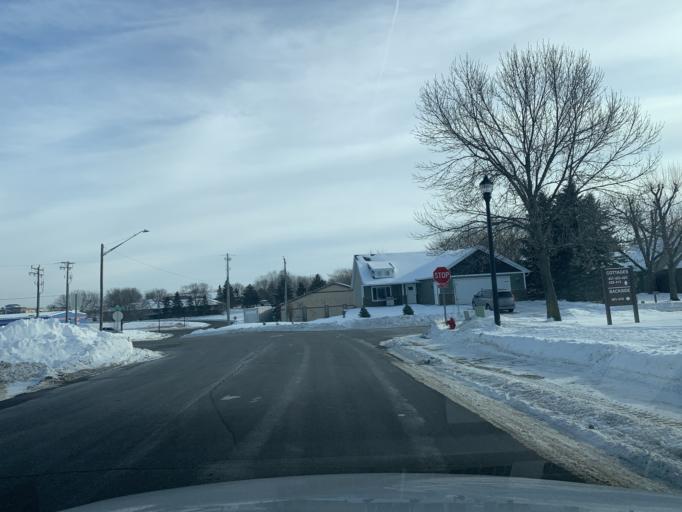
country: US
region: Minnesota
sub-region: Wright County
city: Saint Michael
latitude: 45.2088
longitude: -93.6556
